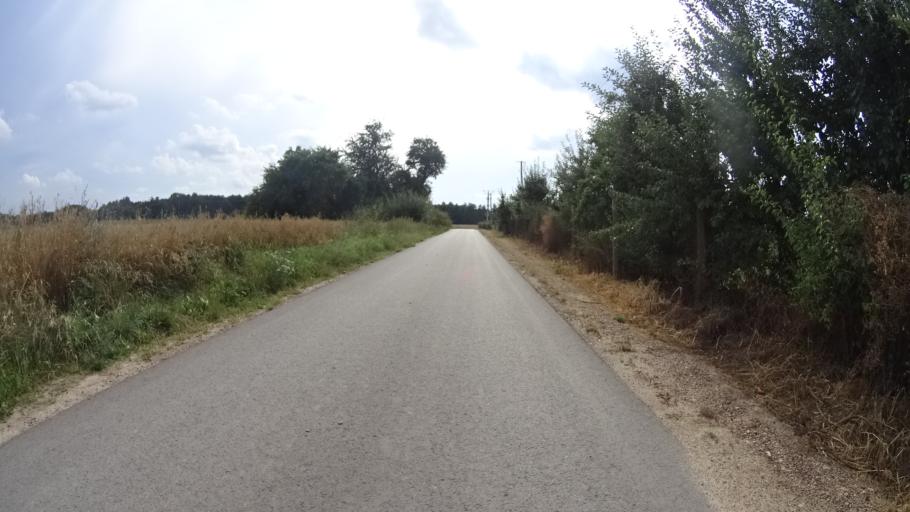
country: PL
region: Masovian Voivodeship
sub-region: Powiat grojecki
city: Goszczyn
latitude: 51.7002
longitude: 20.8191
